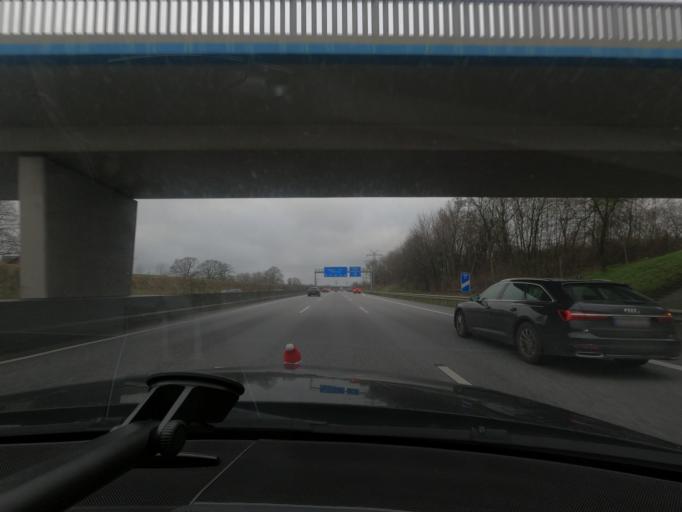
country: DE
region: Schleswig-Holstein
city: Alveslohe
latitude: 53.7991
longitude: 9.9316
